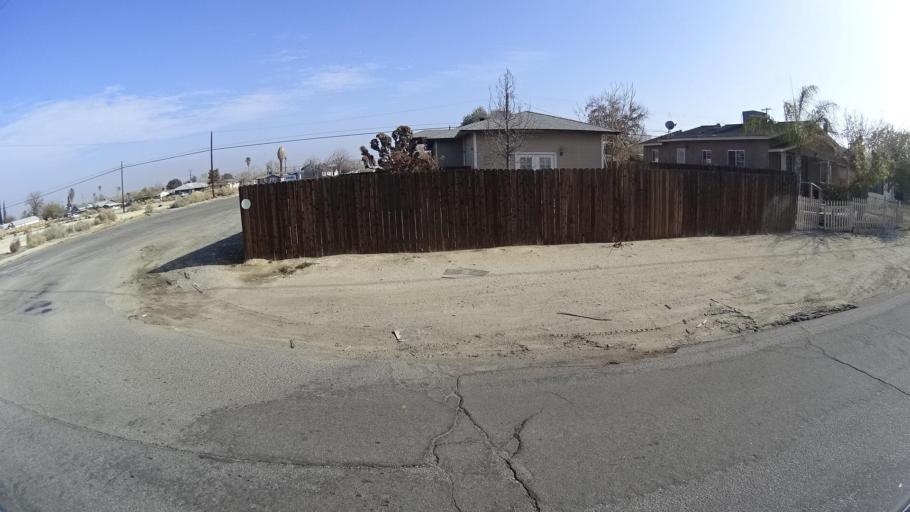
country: US
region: California
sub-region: Kern County
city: Ford City
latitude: 35.1574
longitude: -119.4652
